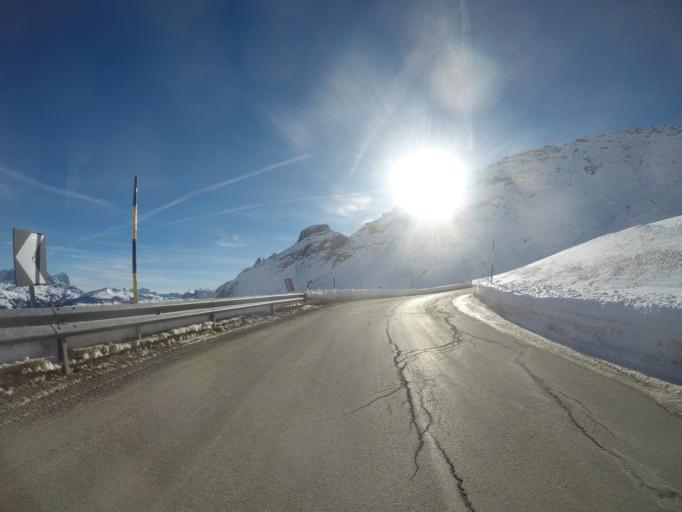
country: IT
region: Trentino-Alto Adige
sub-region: Provincia di Trento
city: Canazei
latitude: 46.4835
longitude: 11.8233
